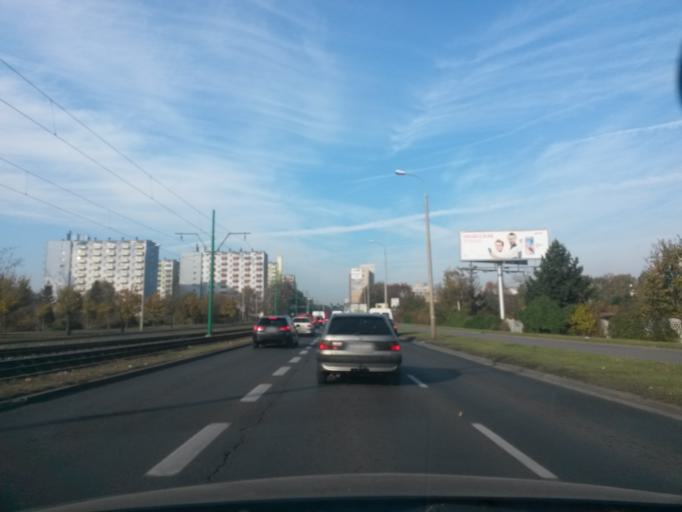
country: PL
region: Greater Poland Voivodeship
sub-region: Poznan
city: Poznan
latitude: 52.3878
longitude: 16.9013
